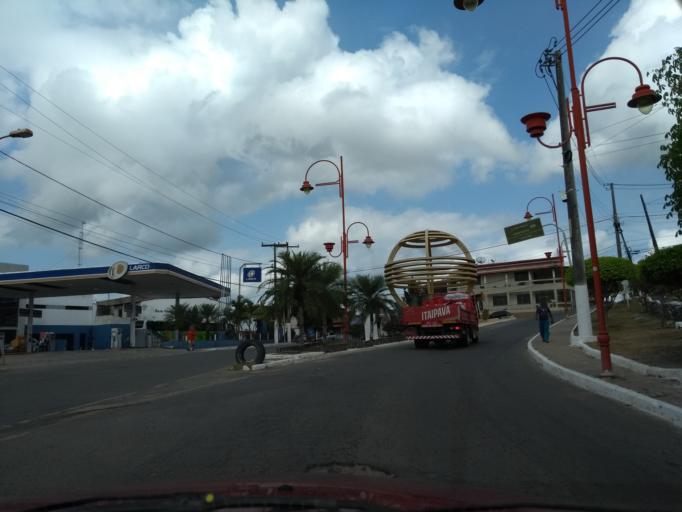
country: BR
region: Bahia
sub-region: Sao Francisco Do Conde
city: Sao Francisco do Conde
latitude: -12.6234
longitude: -38.6737
